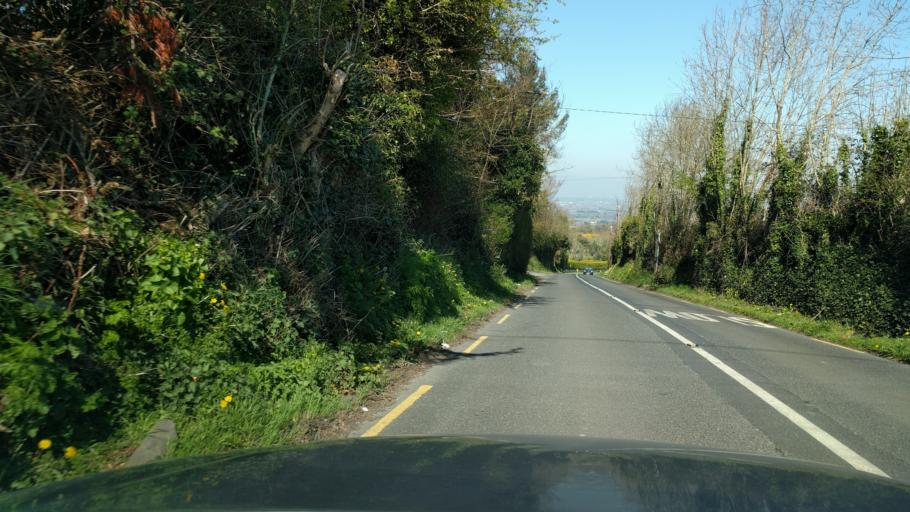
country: IE
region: Leinster
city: Ballyboden
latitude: 53.2584
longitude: -6.3205
